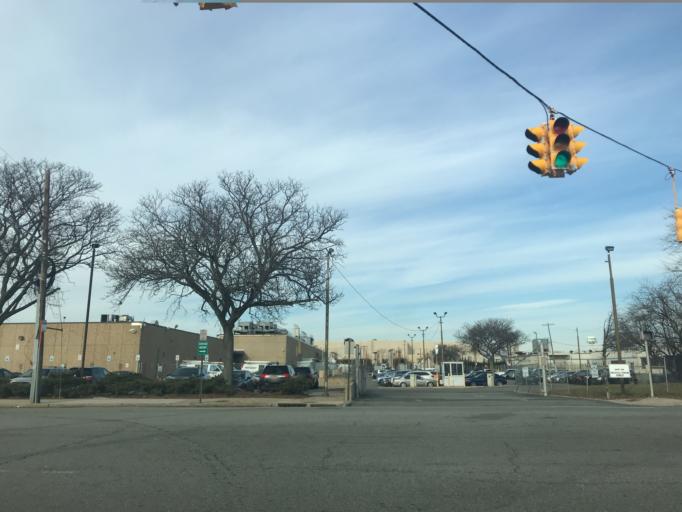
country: US
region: New York
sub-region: Nassau County
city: East Garden City
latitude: 40.7399
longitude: -73.6036
